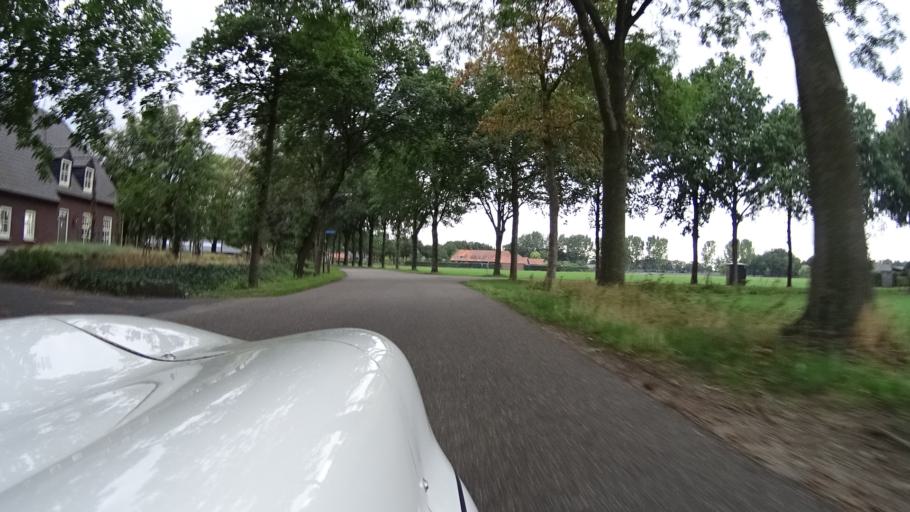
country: NL
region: North Brabant
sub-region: Gemeente Veghel
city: Erp
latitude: 51.6077
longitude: 5.6220
